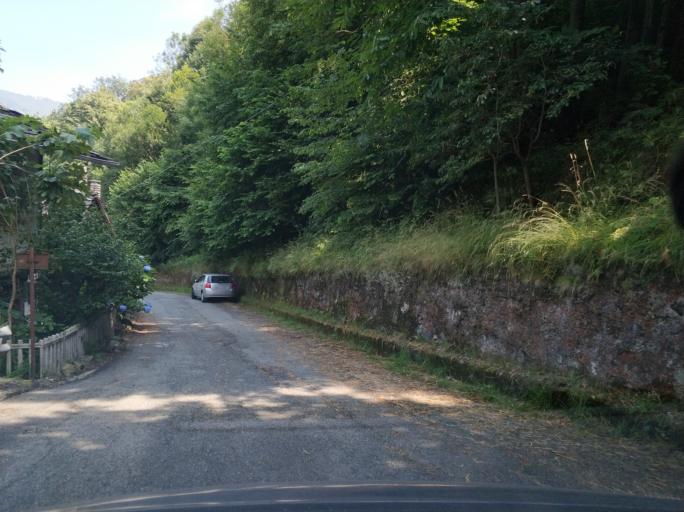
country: IT
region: Piedmont
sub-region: Provincia di Torino
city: Ceres
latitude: 45.3138
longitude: 7.3726
